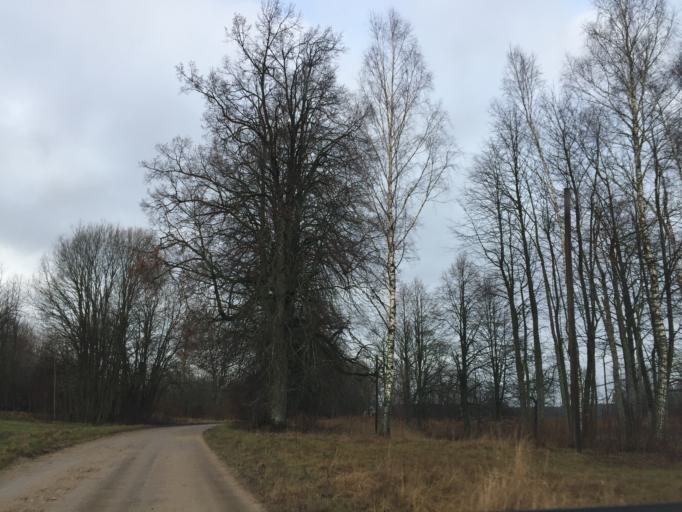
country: LV
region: Vainode
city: Vainode
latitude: 56.6129
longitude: 21.7954
